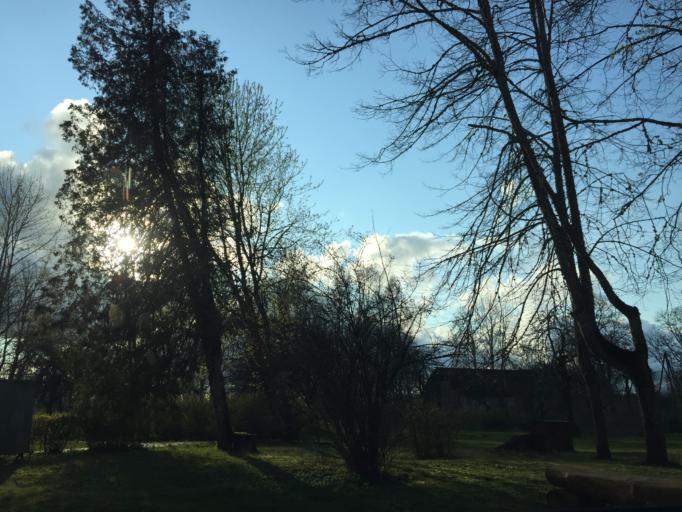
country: LV
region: Aloja
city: Aloja
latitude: 57.6888
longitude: 24.8825
